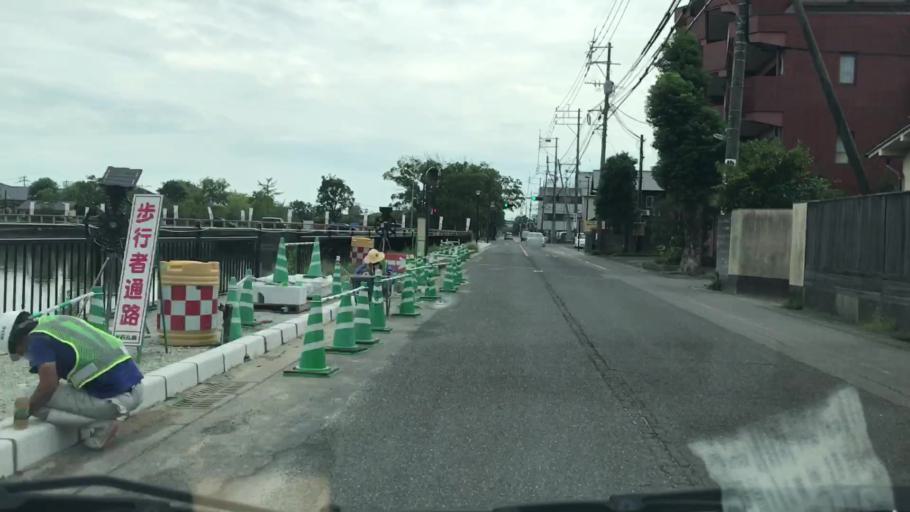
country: JP
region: Saga Prefecture
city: Saga-shi
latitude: 33.2464
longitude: 130.2958
